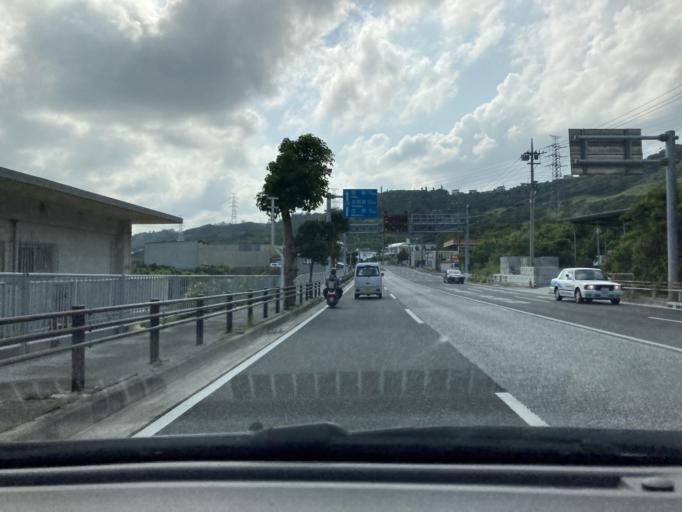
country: JP
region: Okinawa
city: Ginowan
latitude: 26.2720
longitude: 127.7944
